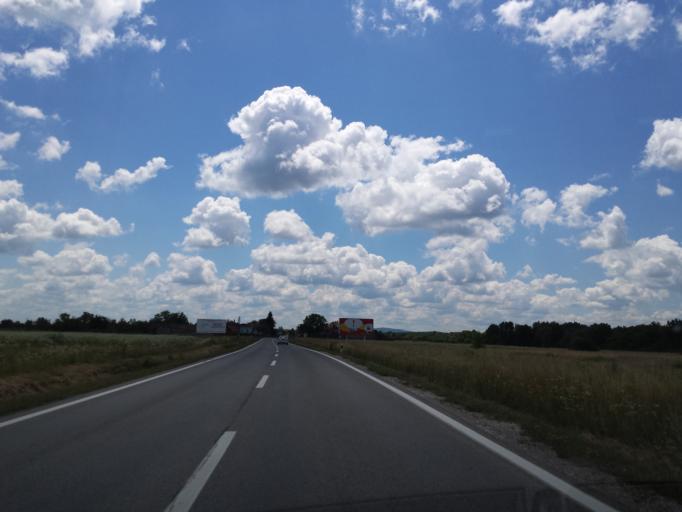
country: HR
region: Sisacko-Moslavacka
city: Lekenik
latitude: 45.5521
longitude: 16.2322
